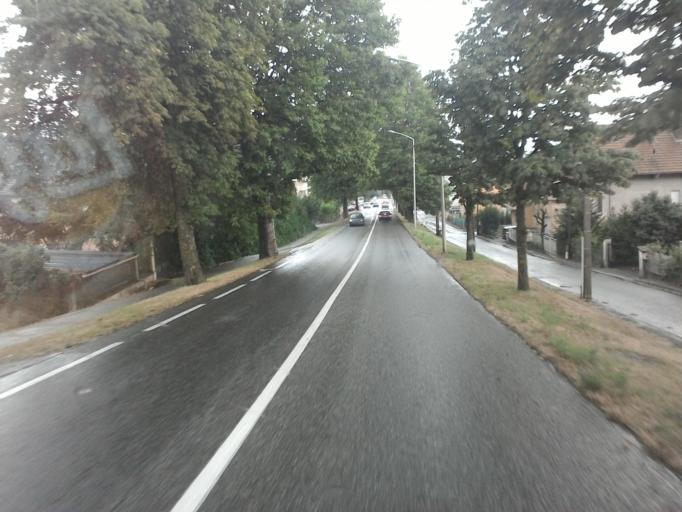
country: FR
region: Provence-Alpes-Cote d'Azur
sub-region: Departement des Hautes-Alpes
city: Gap
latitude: 44.5716
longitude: 6.0830
